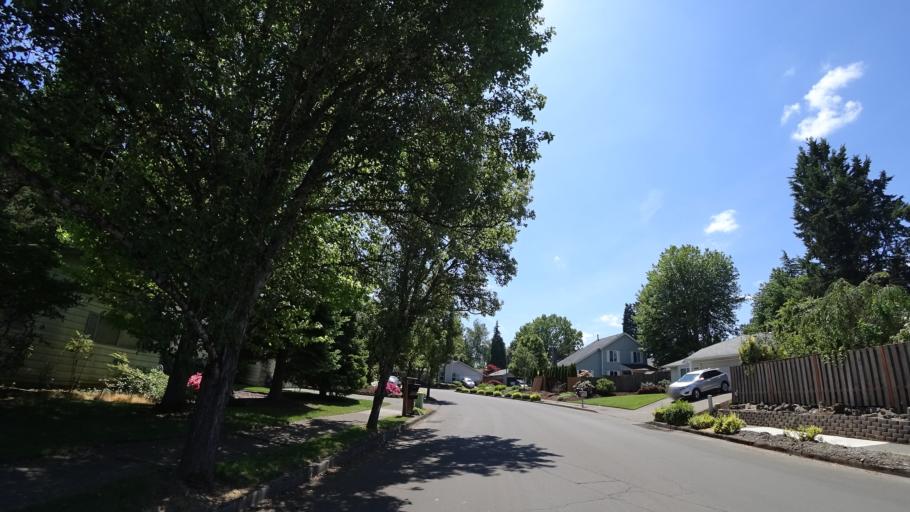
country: US
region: Oregon
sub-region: Washington County
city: Tigard
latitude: 45.4415
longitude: -122.7958
